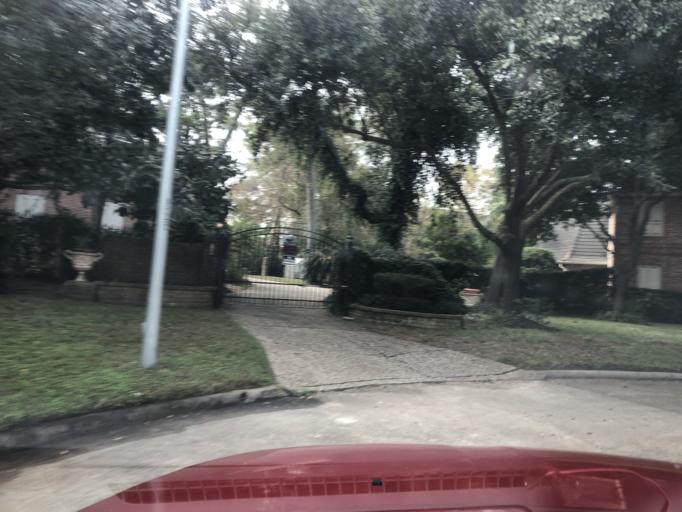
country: US
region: Texas
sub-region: Harris County
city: Spring
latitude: 30.0195
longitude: -95.4678
